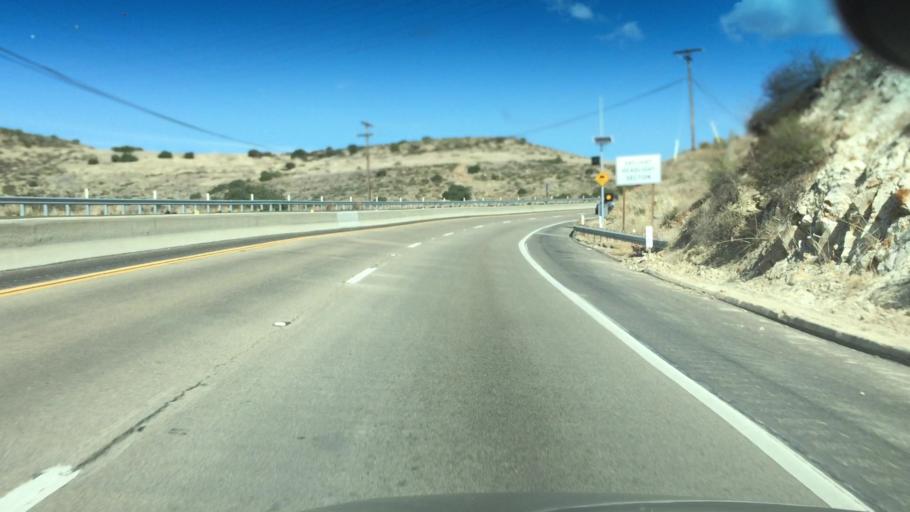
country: US
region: California
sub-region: San Diego County
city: Eucalyptus Hills
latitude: 32.9211
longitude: -116.9479
